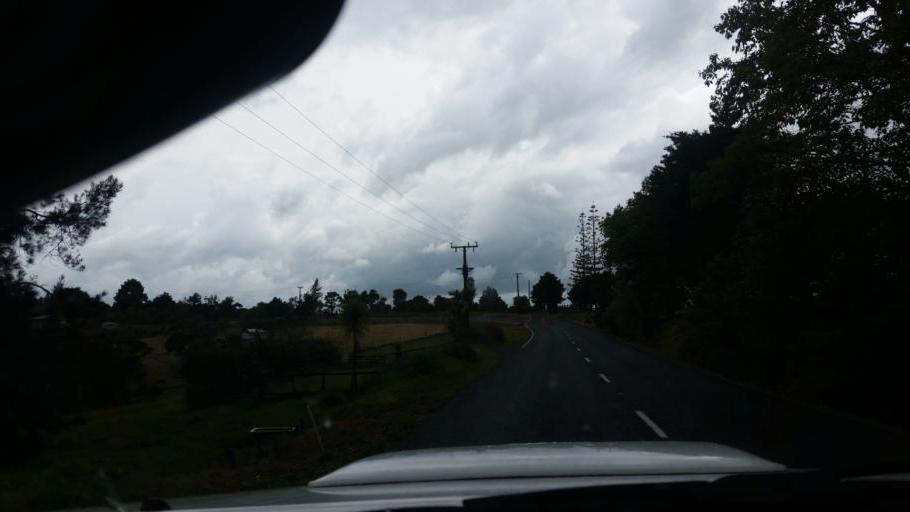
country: NZ
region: Auckland
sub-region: Auckland
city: Wellsford
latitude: -36.1472
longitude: 174.2230
